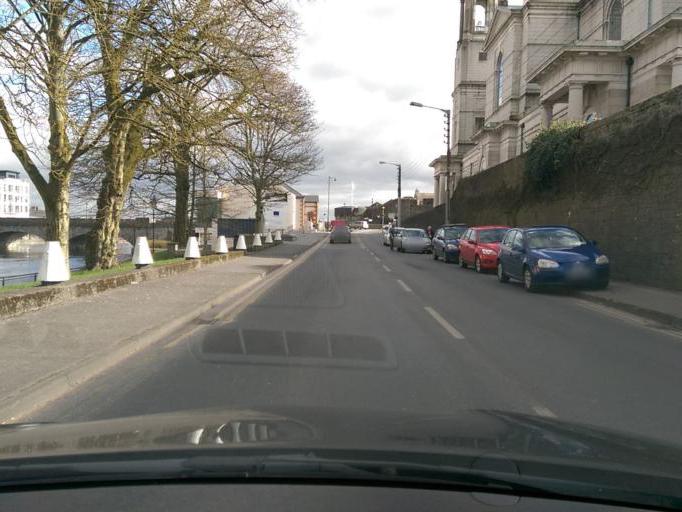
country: IE
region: Leinster
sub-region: An Iarmhi
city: Athlone
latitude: 53.4245
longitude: -7.9439
